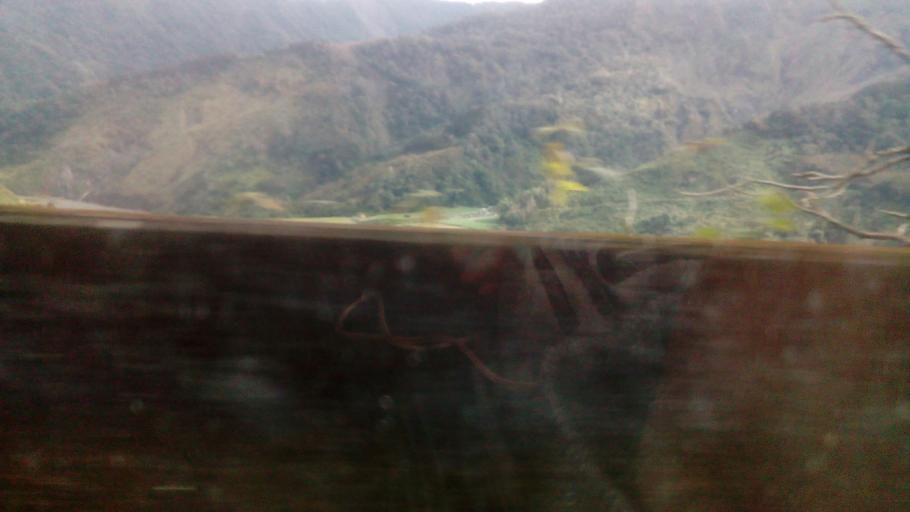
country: TW
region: Taiwan
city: Daxi
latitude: 24.4610
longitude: 121.3946
